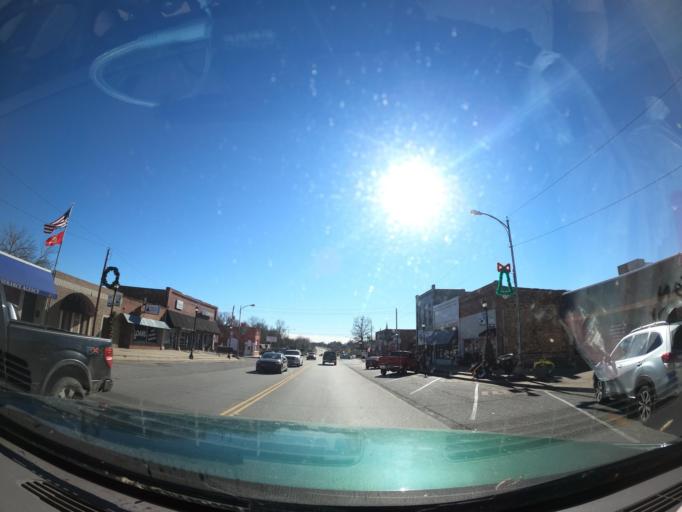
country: US
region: Oklahoma
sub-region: Wagoner County
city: Coweta
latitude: 35.9504
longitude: -95.6506
